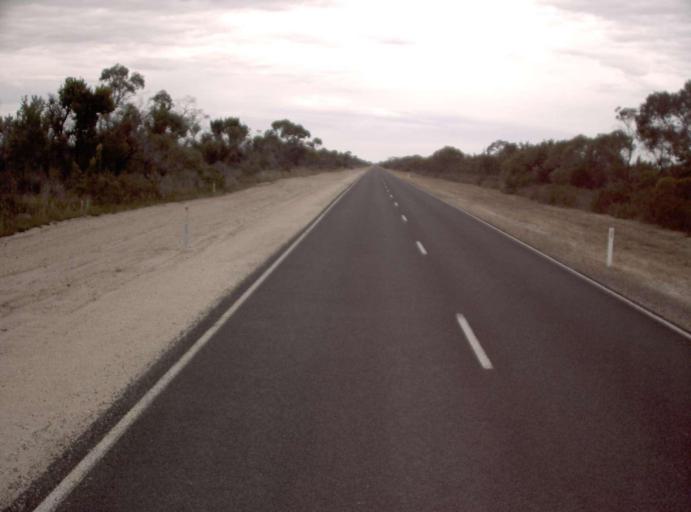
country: AU
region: Victoria
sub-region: East Gippsland
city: Bairnsdale
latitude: -38.1201
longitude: 147.4562
